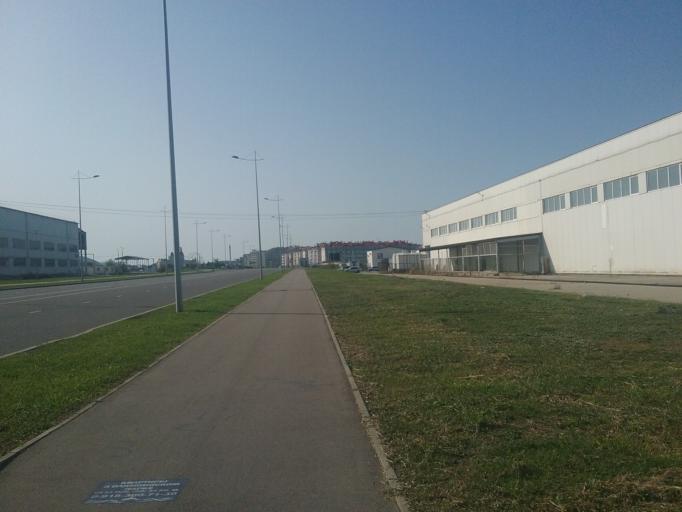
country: RU
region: Krasnodarskiy
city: Vysokoye
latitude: 43.3971
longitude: 39.9863
